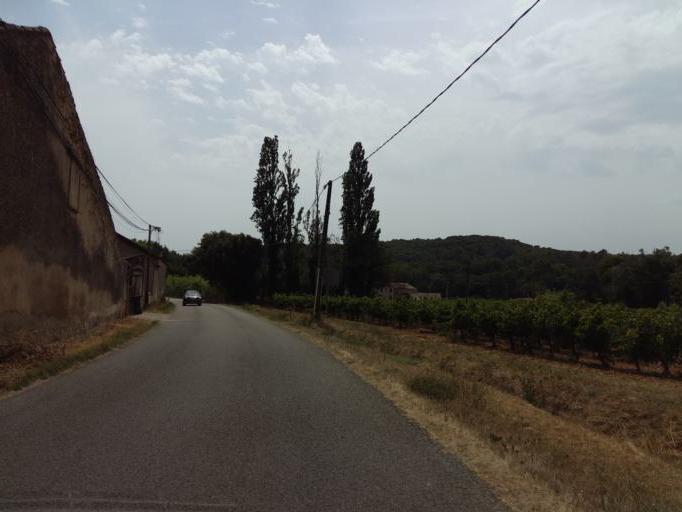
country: FR
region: Provence-Alpes-Cote d'Azur
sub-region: Departement du Vaucluse
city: Piolenc
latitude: 44.1955
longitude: 4.7792
